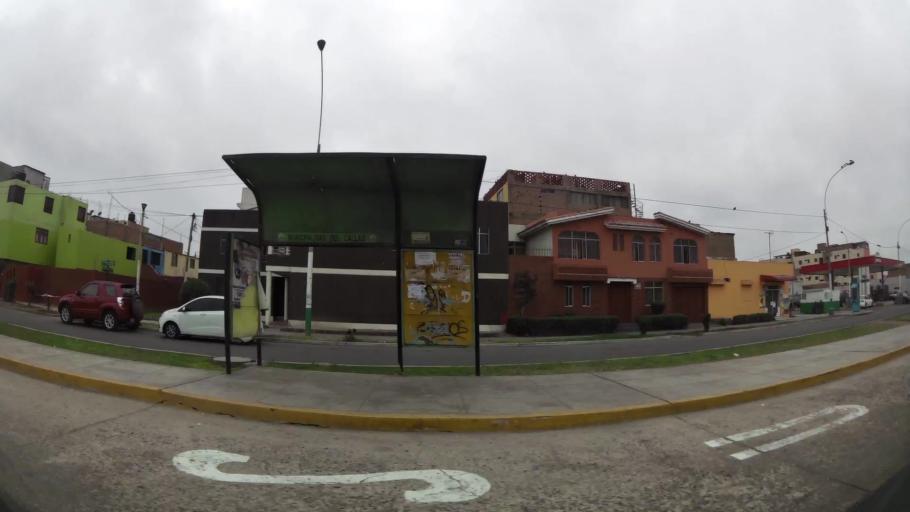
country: PE
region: Callao
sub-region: Callao
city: Callao
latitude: -12.0674
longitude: -77.1165
